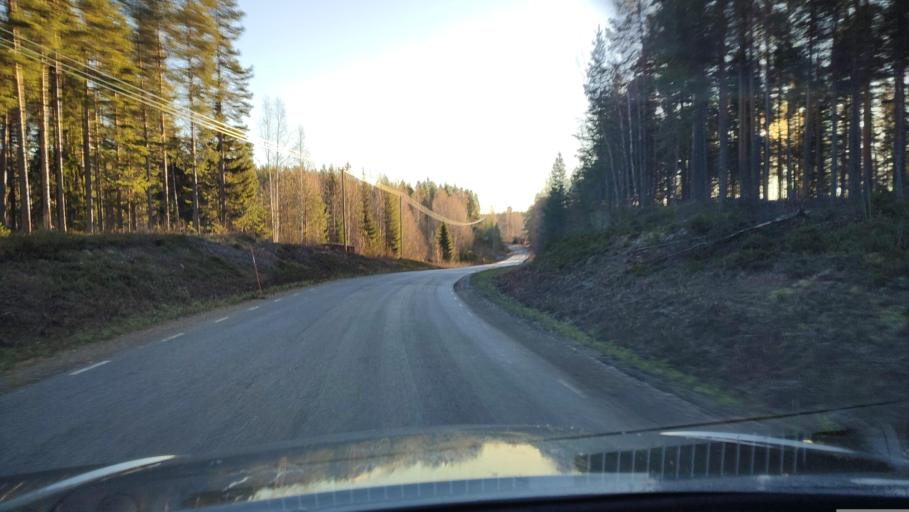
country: SE
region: Vaesterbotten
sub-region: Skelleftea Kommun
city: Viken
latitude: 64.7004
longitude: 20.9089
